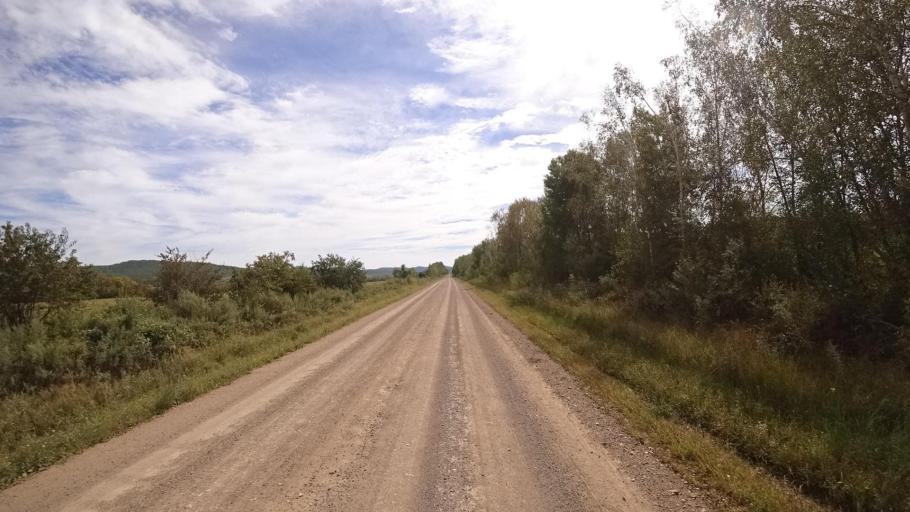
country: RU
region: Primorskiy
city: Yakovlevka
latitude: 44.6142
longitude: 133.5987
